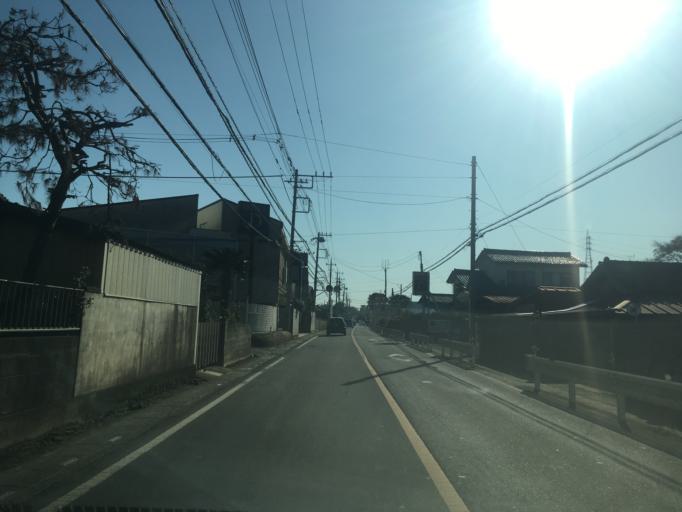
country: JP
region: Saitama
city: Kamifukuoka
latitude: 35.8609
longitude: 139.4704
